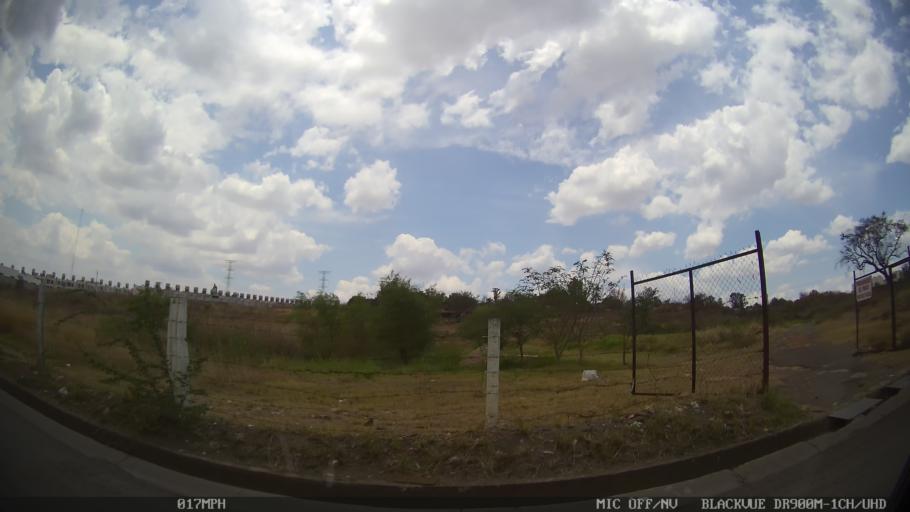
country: MX
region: Jalisco
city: Tonala
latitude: 20.6432
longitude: -103.2273
